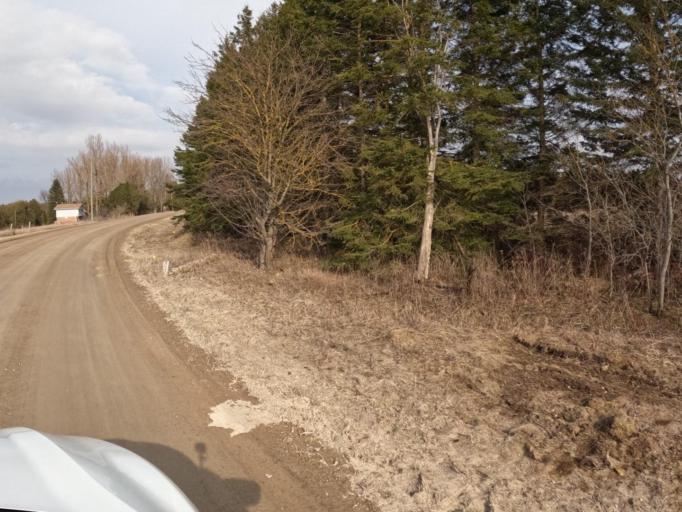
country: CA
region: Ontario
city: Orangeville
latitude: 43.9136
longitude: -80.2622
